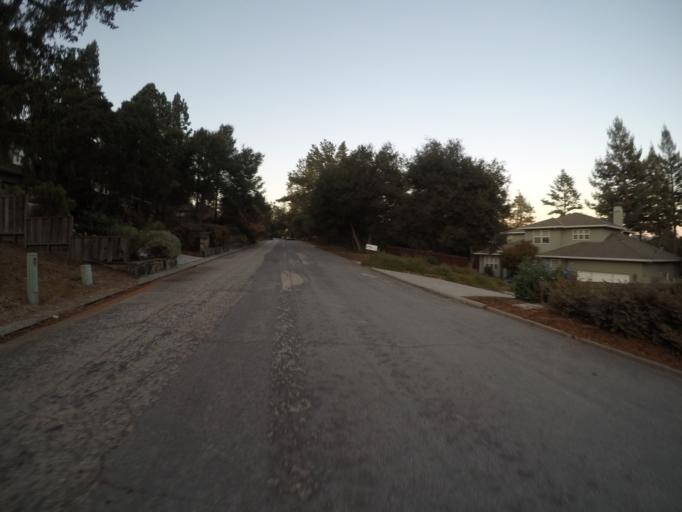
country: US
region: California
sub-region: Santa Cruz County
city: Mount Hermon
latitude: 37.0426
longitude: -122.0392
